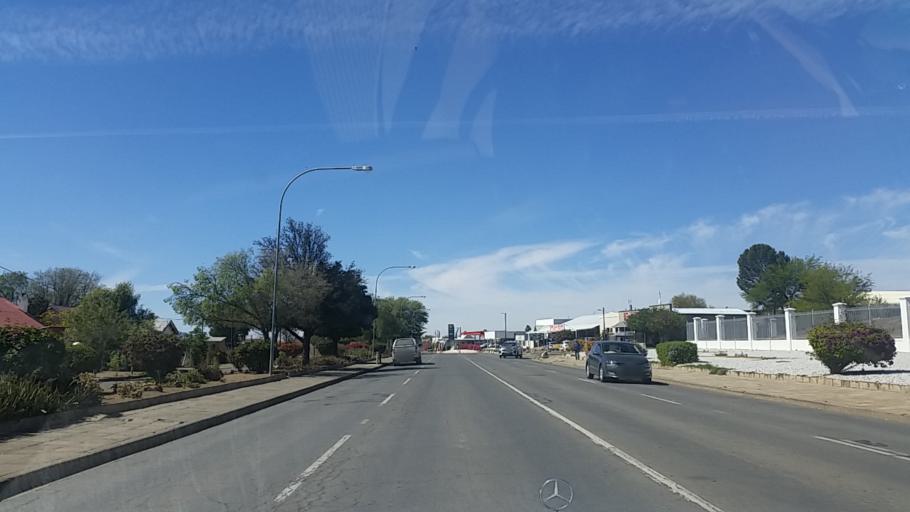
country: ZA
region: Eastern Cape
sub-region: Cacadu District Municipality
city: Graaff-Reinet
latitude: -32.2627
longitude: 24.5404
